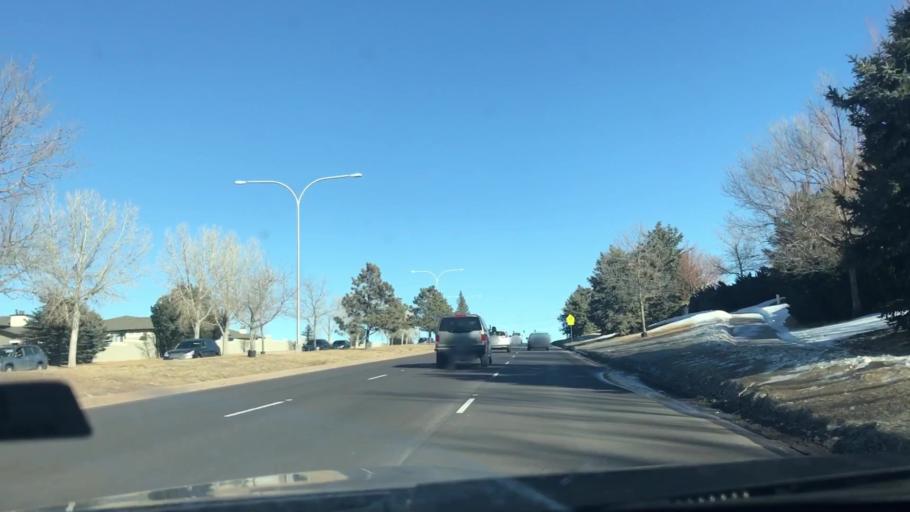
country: US
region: Colorado
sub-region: El Paso County
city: Air Force Academy
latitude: 38.9669
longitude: -104.7801
